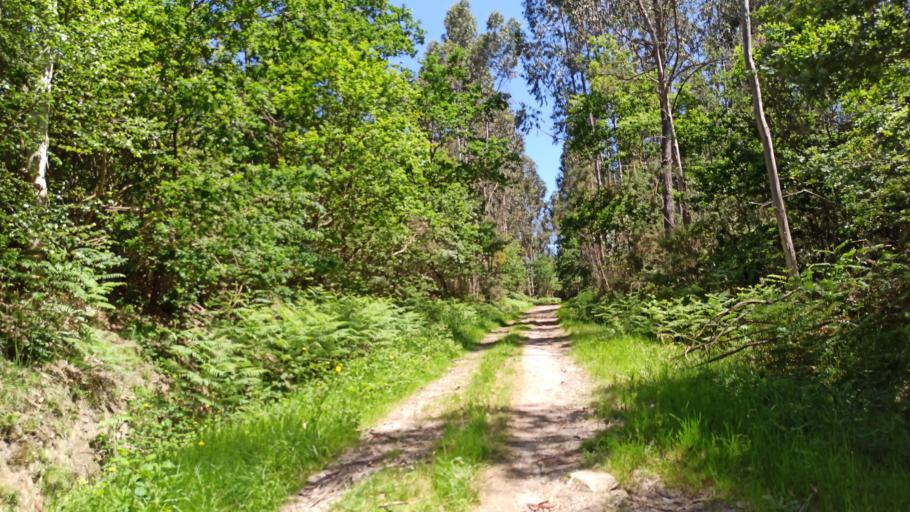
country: ES
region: Galicia
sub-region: Provincia da Coruna
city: Negreira
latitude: 42.9202
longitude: -8.7209
